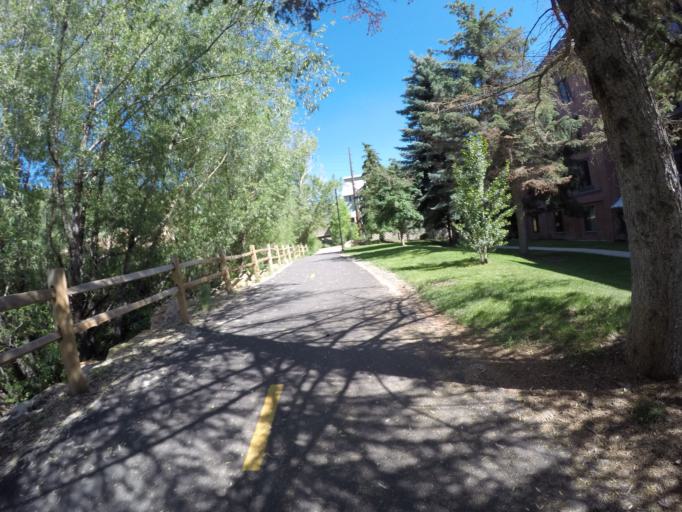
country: US
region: Utah
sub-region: Summit County
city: Park City
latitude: 40.6494
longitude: -111.4989
